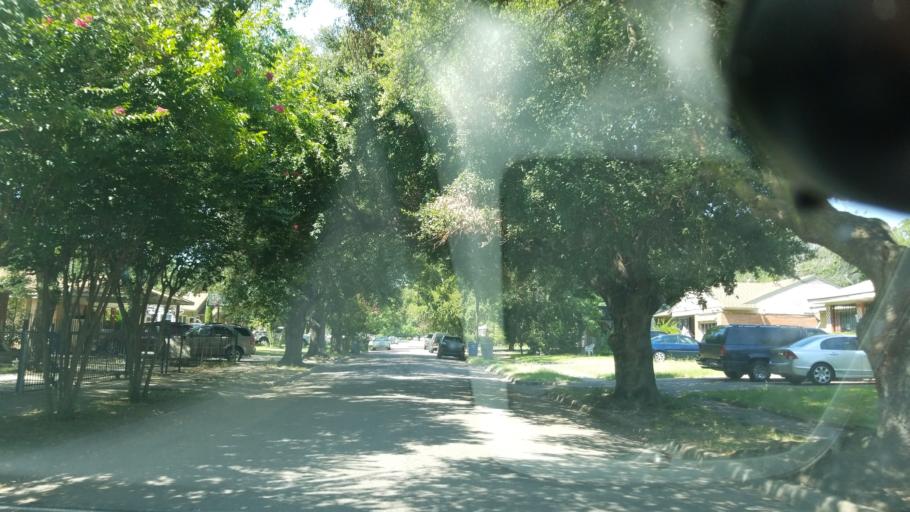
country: US
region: Texas
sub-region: Dallas County
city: Cockrell Hill
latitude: 32.7155
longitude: -96.8352
